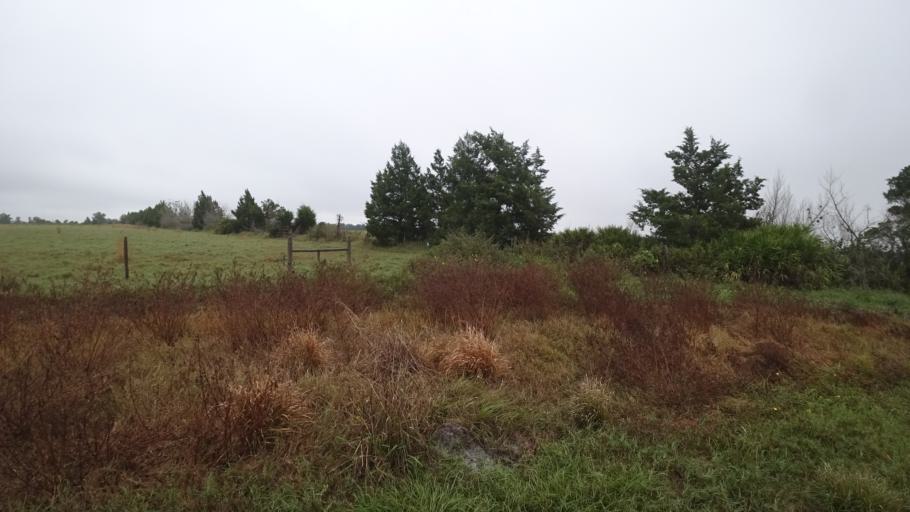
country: US
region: Florida
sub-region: Sarasota County
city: Warm Mineral Springs
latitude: 27.3055
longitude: -82.1550
